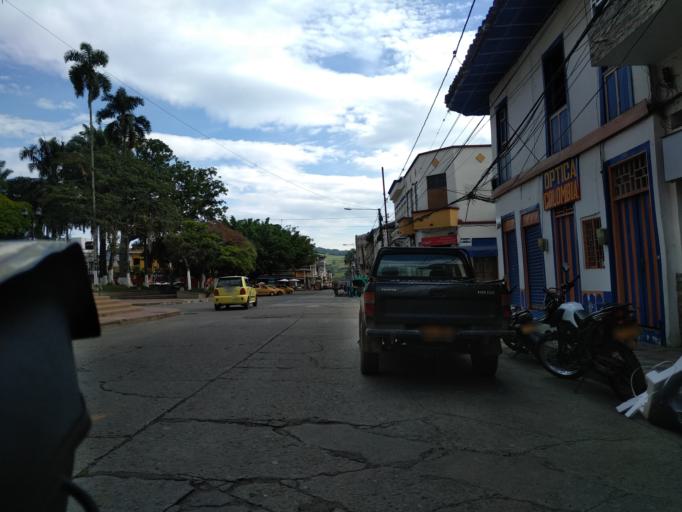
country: CO
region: Valle del Cauca
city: Caicedonia
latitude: 4.3312
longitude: -75.8285
